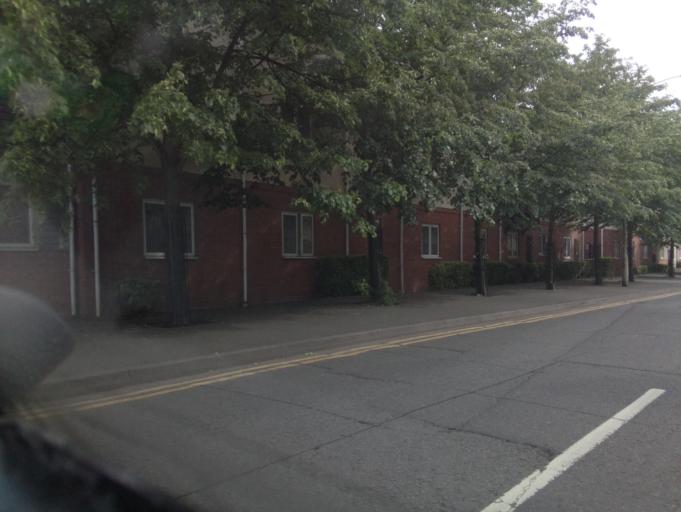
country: GB
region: England
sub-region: Worcestershire
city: Evesham
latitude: 52.0927
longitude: -1.9434
